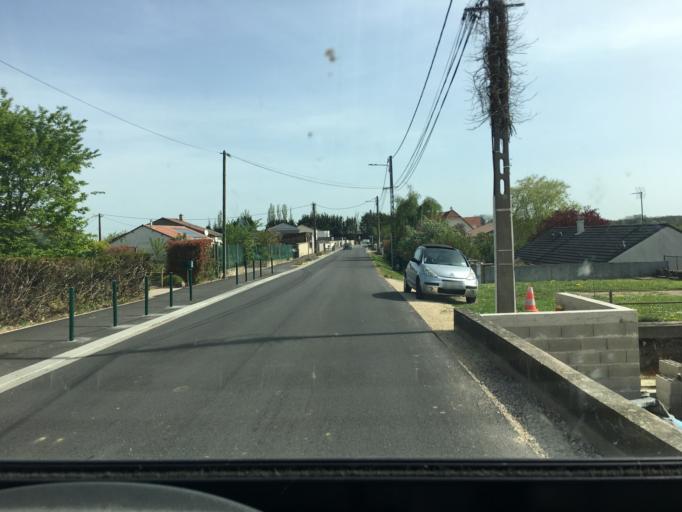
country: FR
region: Lorraine
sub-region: Departement de Meurthe-et-Moselle
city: Gondreville
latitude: 48.6591
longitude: 5.9808
